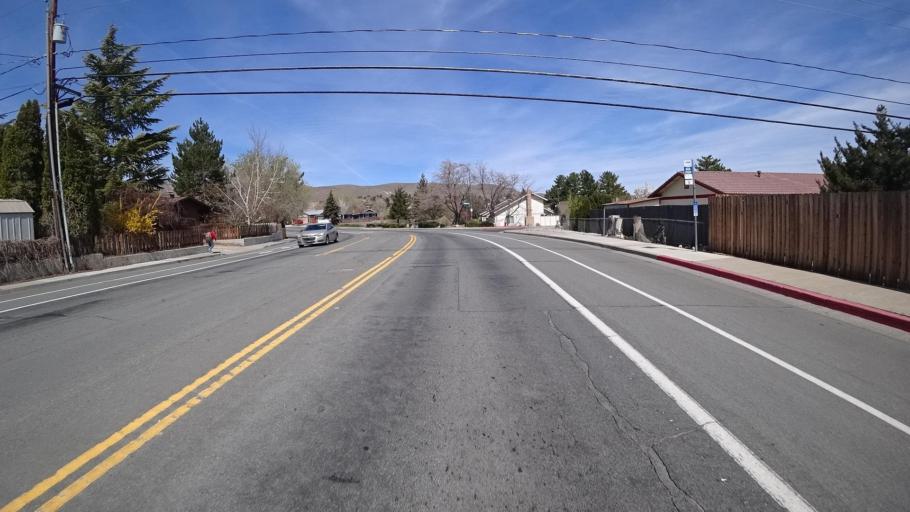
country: US
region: Nevada
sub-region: Washoe County
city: Reno
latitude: 39.5334
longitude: -119.8586
